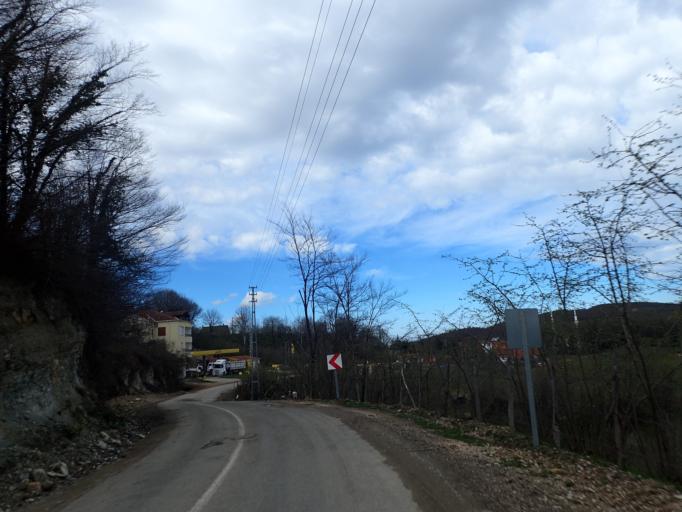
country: TR
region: Ordu
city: Kumru
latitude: 40.9386
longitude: 37.2615
